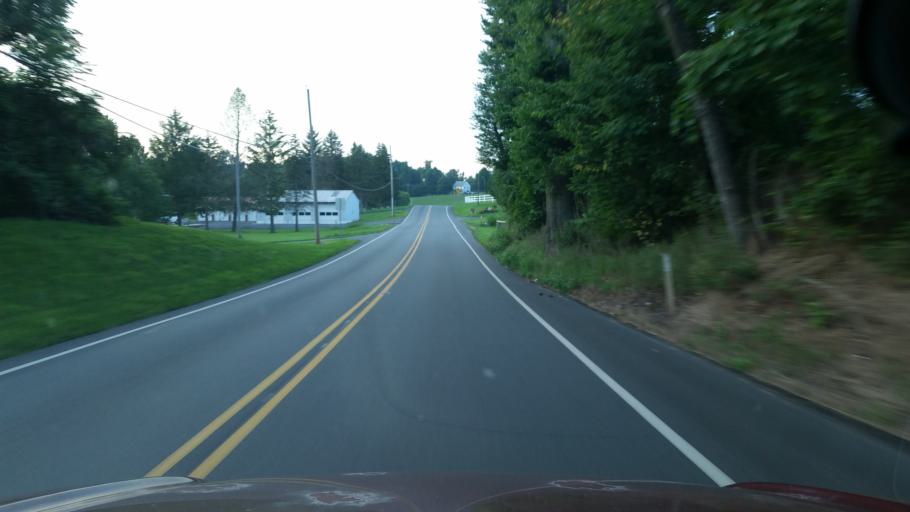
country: US
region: Pennsylvania
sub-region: Lebanon County
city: Campbelltown
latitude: 40.2653
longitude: -76.5577
